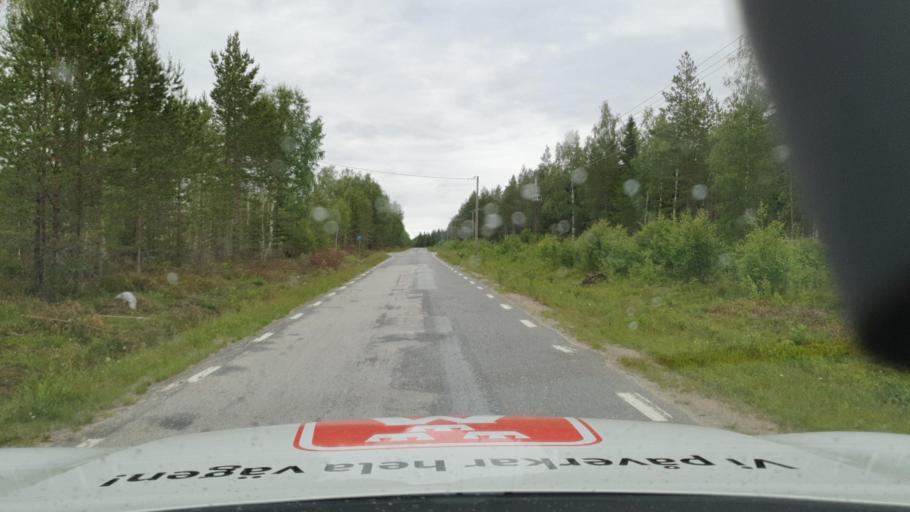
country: SE
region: Vaesterbotten
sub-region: Nordmalings Kommun
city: Nordmaling
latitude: 63.4559
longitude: 19.4672
